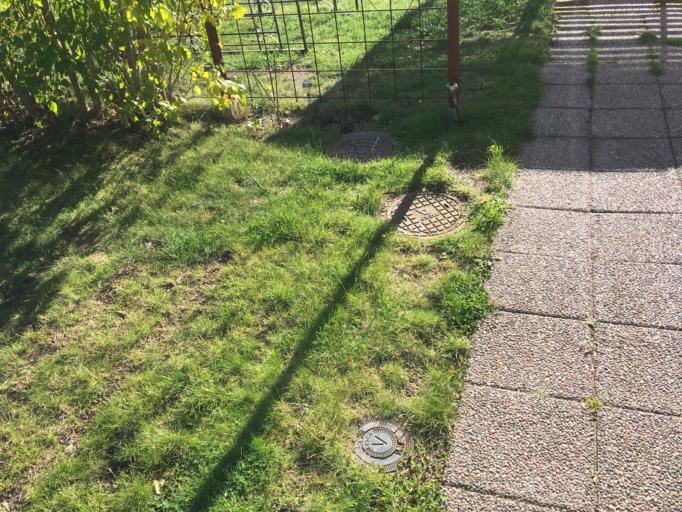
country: SE
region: Vaermland
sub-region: Hammaro Kommun
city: Skoghall
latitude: 59.3236
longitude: 13.4619
